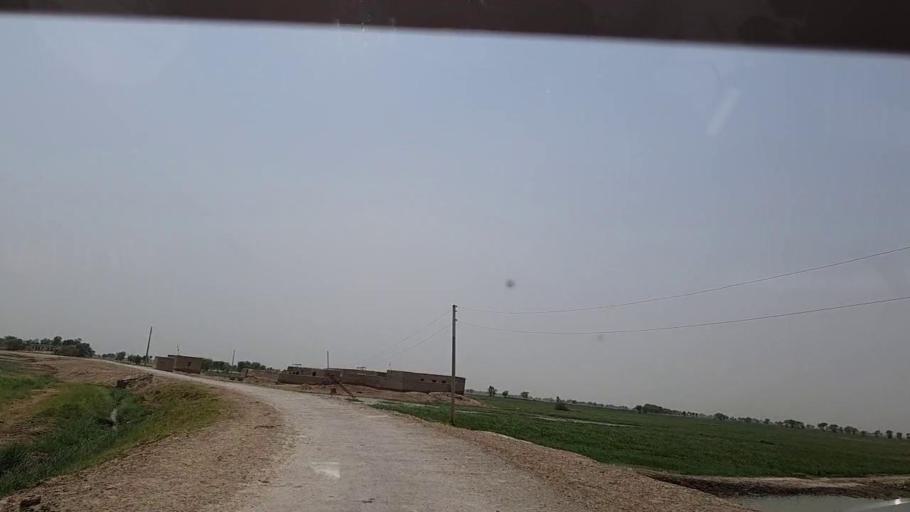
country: PK
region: Sindh
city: Khairpur Nathan Shah
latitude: 27.0093
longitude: 67.6550
